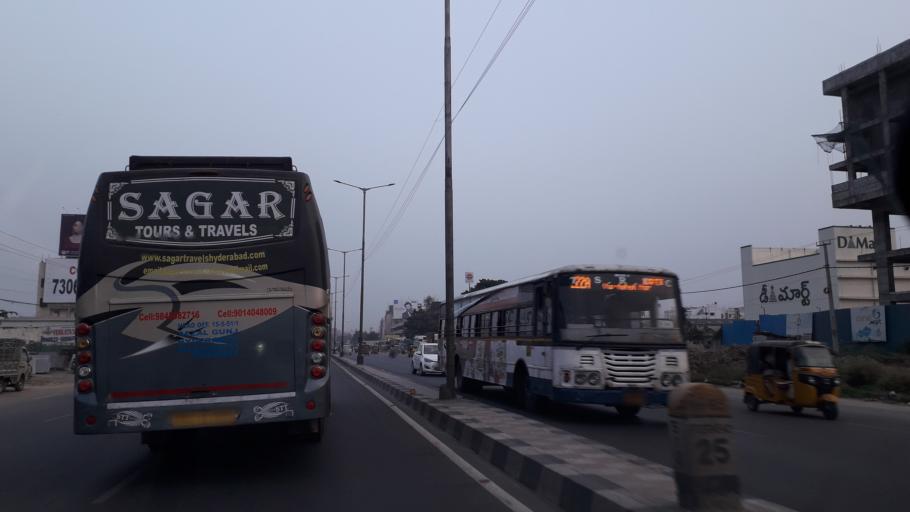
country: IN
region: Telangana
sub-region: Medak
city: Serilingampalle
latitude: 17.5112
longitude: 78.2953
